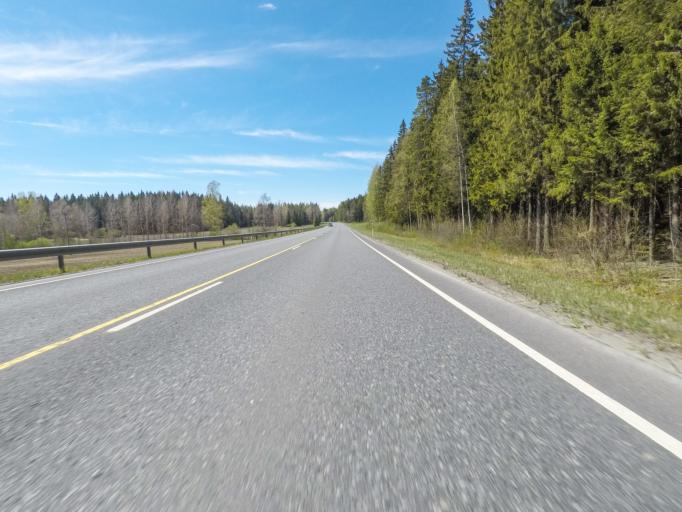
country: FI
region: Haeme
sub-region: Forssa
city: Humppila
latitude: 60.9789
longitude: 23.4304
